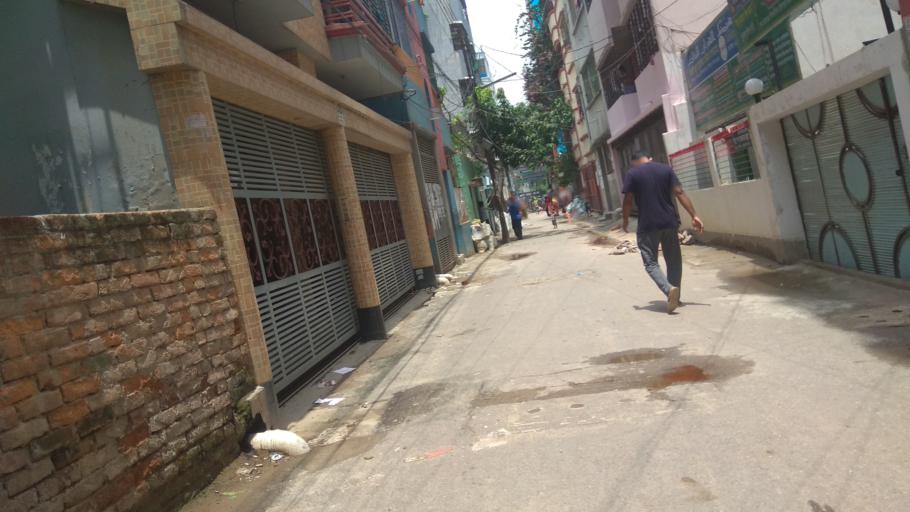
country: BD
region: Dhaka
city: Tungi
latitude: 23.8182
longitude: 90.3550
